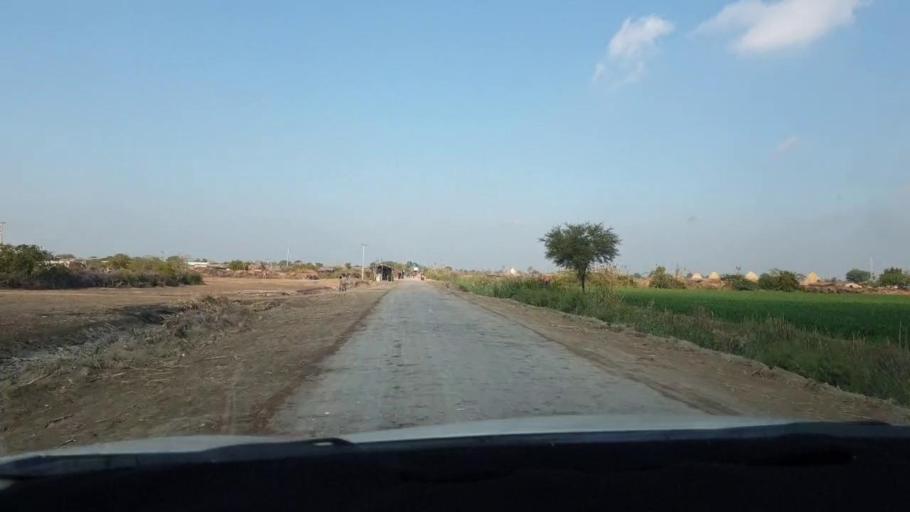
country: PK
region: Sindh
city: Berani
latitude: 25.7983
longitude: 68.8366
